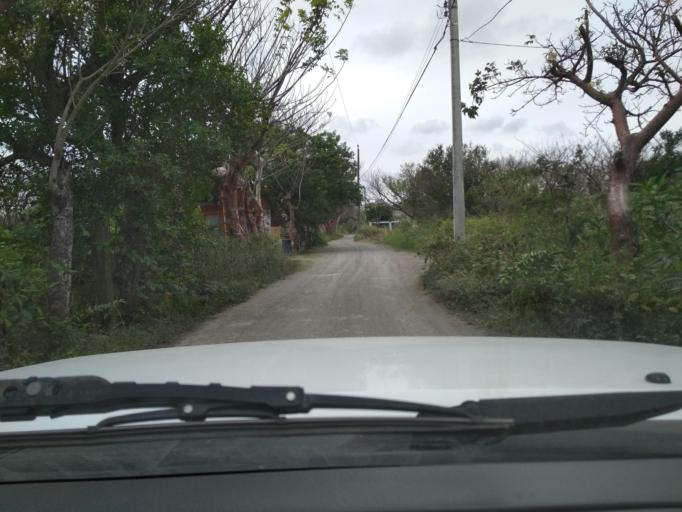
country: MX
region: Veracruz
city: El Tejar
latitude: 19.0639
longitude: -96.1384
